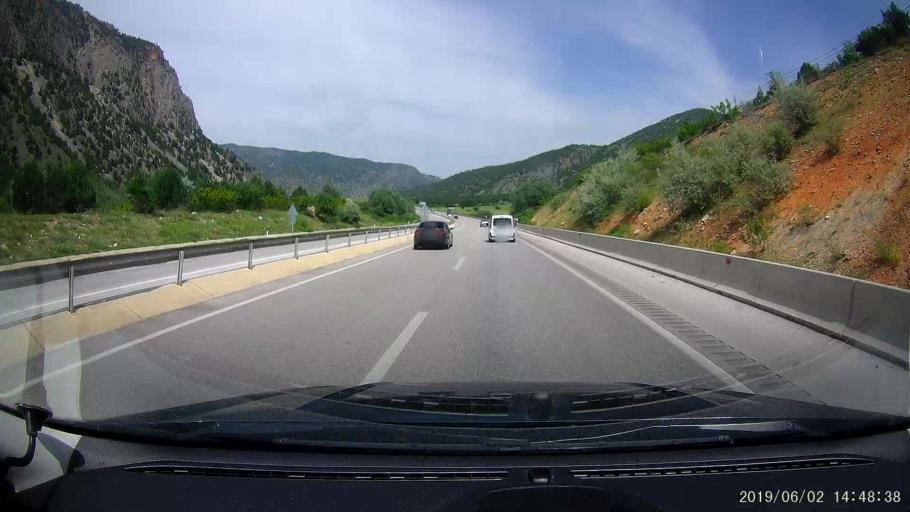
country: TR
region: Corum
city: Hacihamza
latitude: 41.0624
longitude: 34.4848
